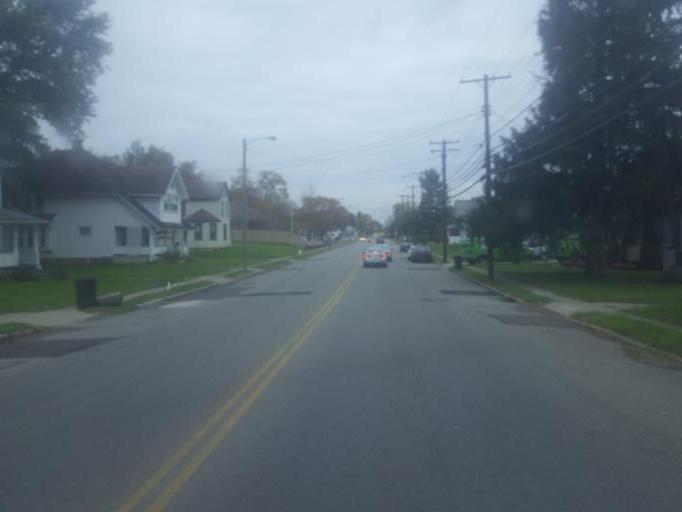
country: US
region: Ohio
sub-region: Richland County
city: Mansfield
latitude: 40.7470
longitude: -82.5066
